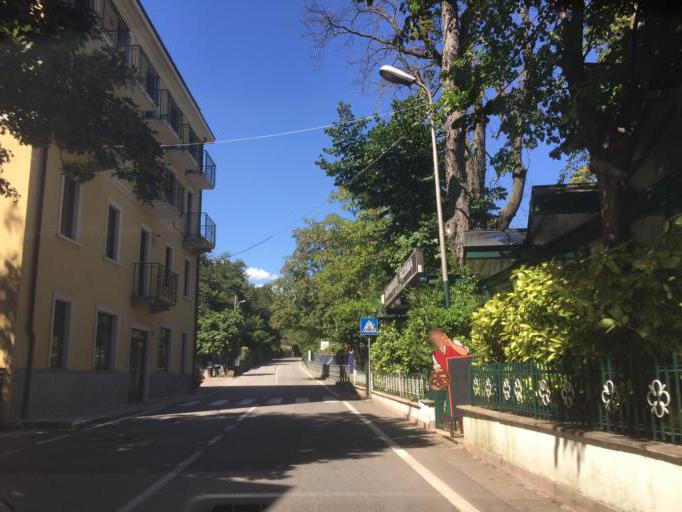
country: IT
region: Lombardy
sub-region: Provincia di Varese
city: Porto Ceresio
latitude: 45.9112
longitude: 8.8980
